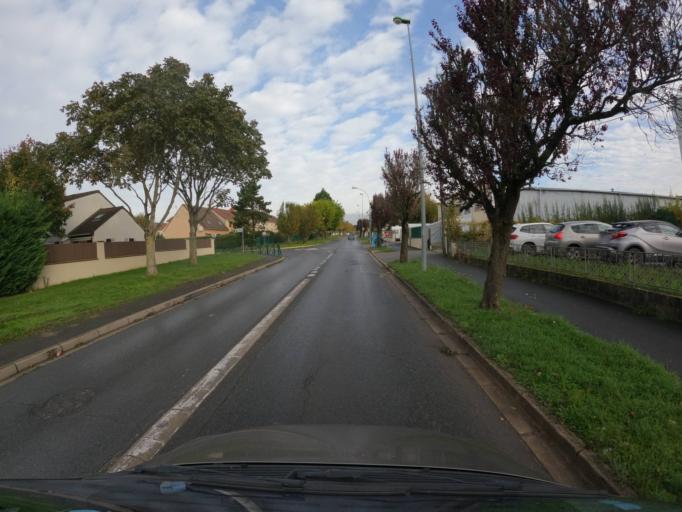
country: FR
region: Ile-de-France
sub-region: Departement de Seine-et-Marne
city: Courtry
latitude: 48.9085
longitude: 2.6032
